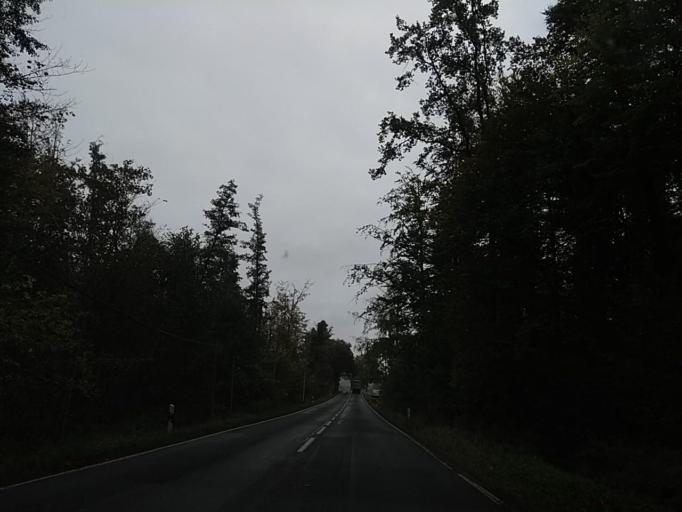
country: DE
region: Mecklenburg-Vorpommern
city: Kropelin
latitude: 54.0518
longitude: 11.7991
